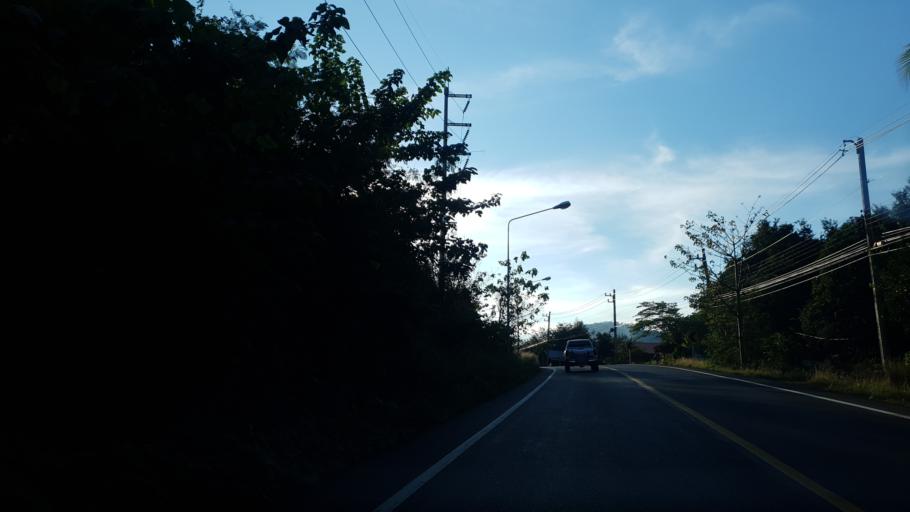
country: TH
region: Loei
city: Dan Sai
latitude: 17.2306
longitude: 101.0492
